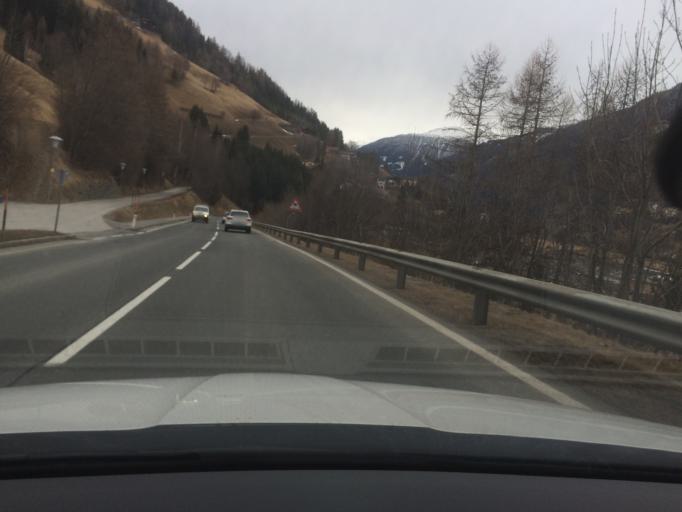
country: AT
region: Tyrol
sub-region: Politischer Bezirk Lienz
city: Matrei in Osttirol
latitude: 46.9986
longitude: 12.5430
